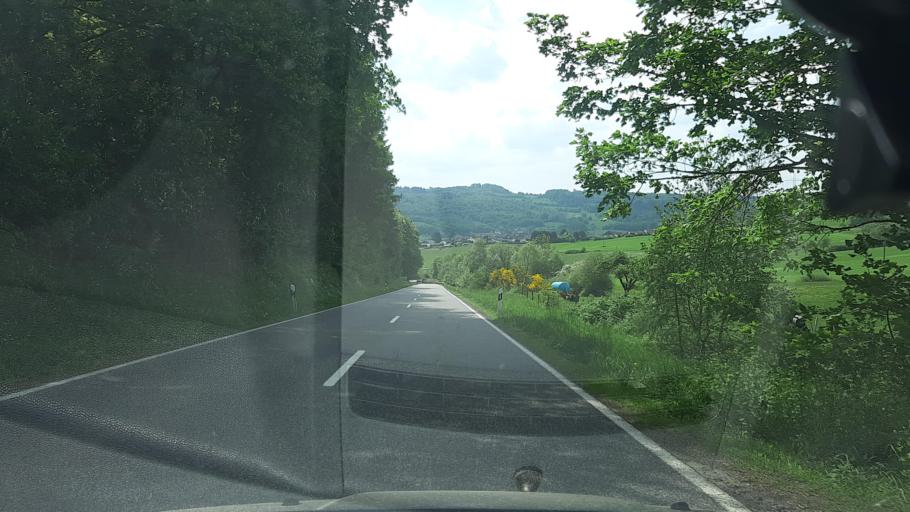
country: DE
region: Hesse
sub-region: Regierungsbezirk Giessen
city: Greifenstein
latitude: 50.6003
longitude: 8.2983
